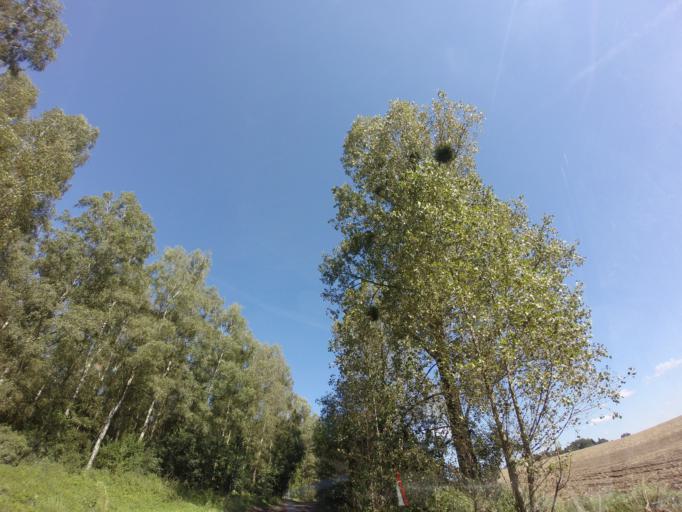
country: PL
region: West Pomeranian Voivodeship
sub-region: Powiat choszczenski
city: Recz
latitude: 53.1654
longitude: 15.5758
